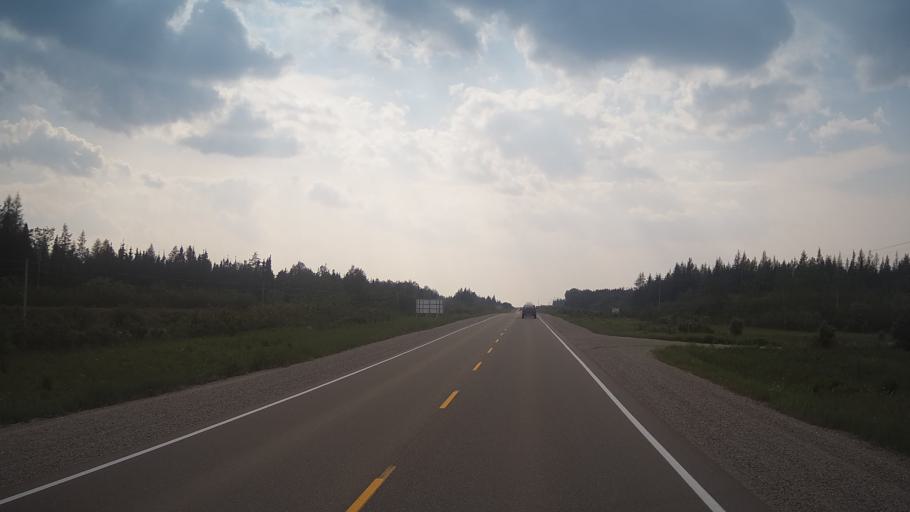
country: CA
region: Ontario
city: Kapuskasing
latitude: 49.4631
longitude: -82.6159
